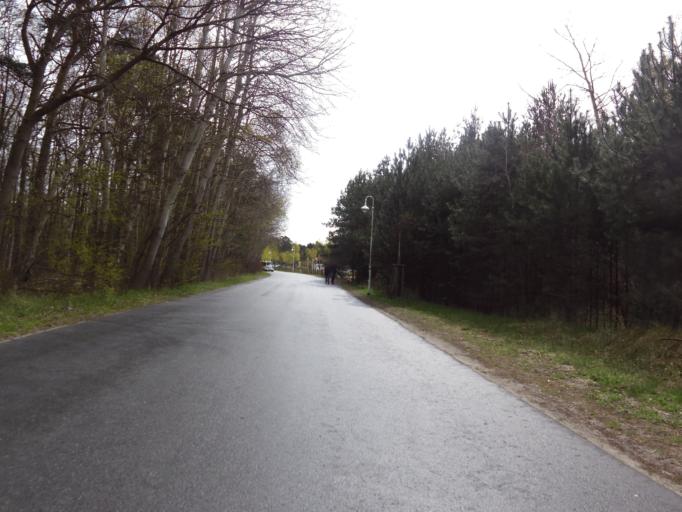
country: DE
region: Mecklenburg-Vorpommern
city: Ostseebad Prerow
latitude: 54.4530
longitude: 12.5519
